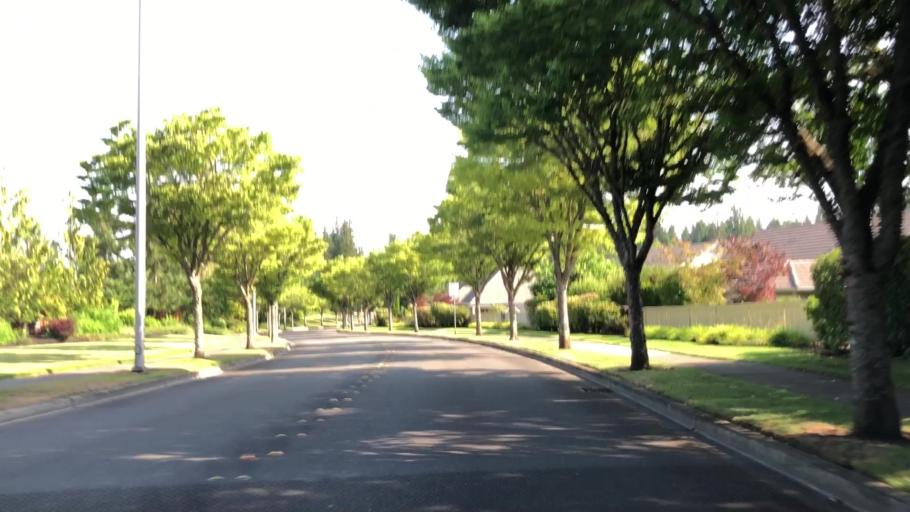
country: US
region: Washington
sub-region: Thurston County
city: Tanglewilde-Thompson Place
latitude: 47.0909
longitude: -122.7593
